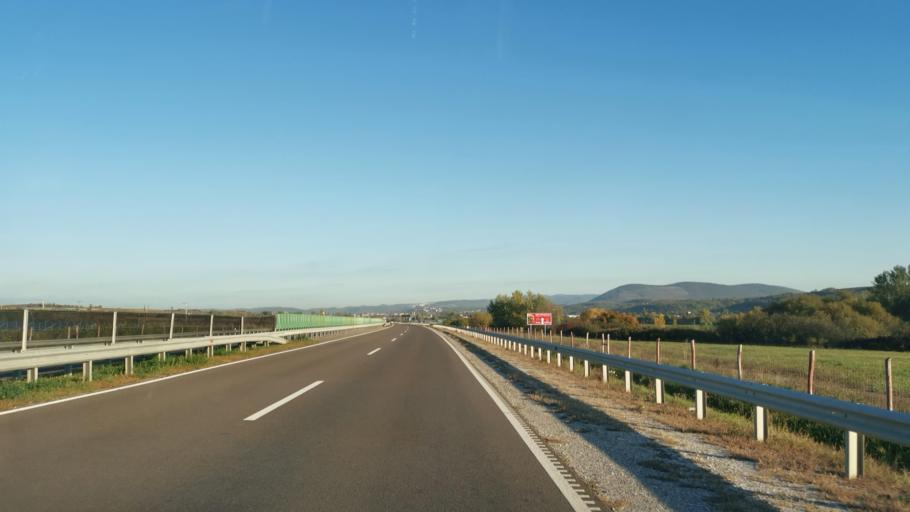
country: HU
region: Heves
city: Andornaktalya
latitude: 47.8526
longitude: 20.3985
